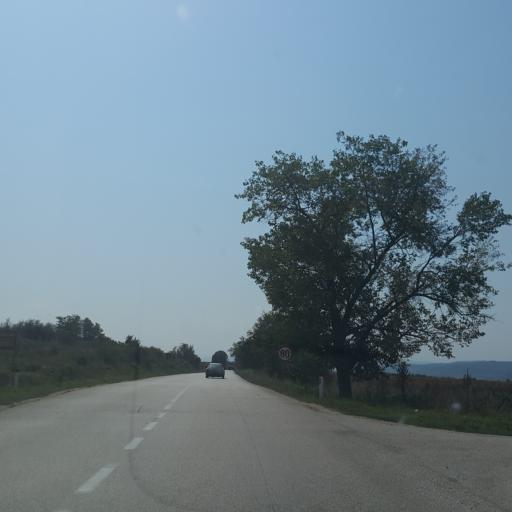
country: RS
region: Central Serbia
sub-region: Zajecarski Okrug
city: Knjazevac
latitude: 43.6775
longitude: 22.2894
